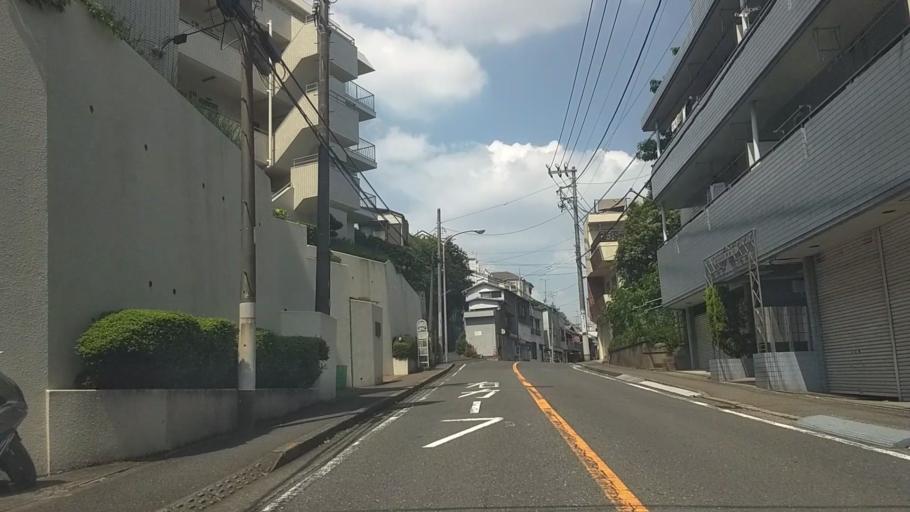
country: JP
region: Kanagawa
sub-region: Kawasaki-shi
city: Kawasaki
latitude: 35.5109
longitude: 139.6720
